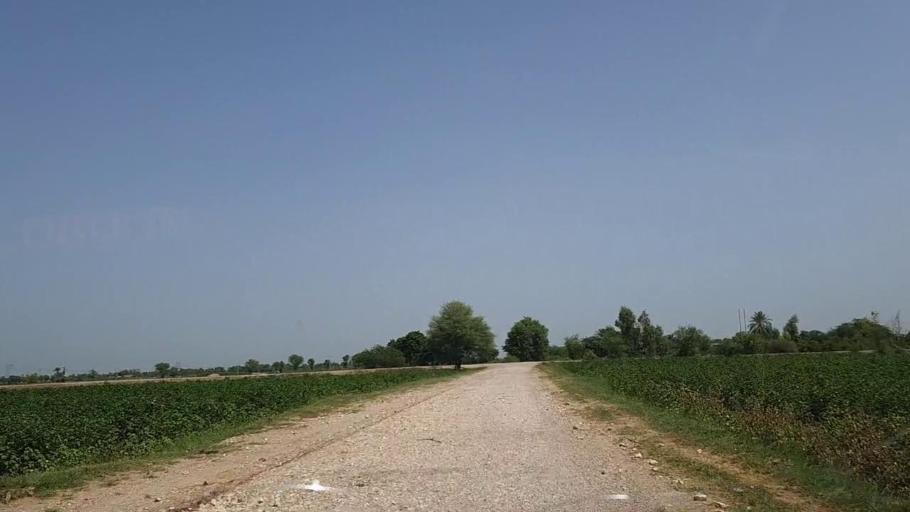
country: PK
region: Sindh
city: Kandiaro
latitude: 27.0128
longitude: 68.1722
